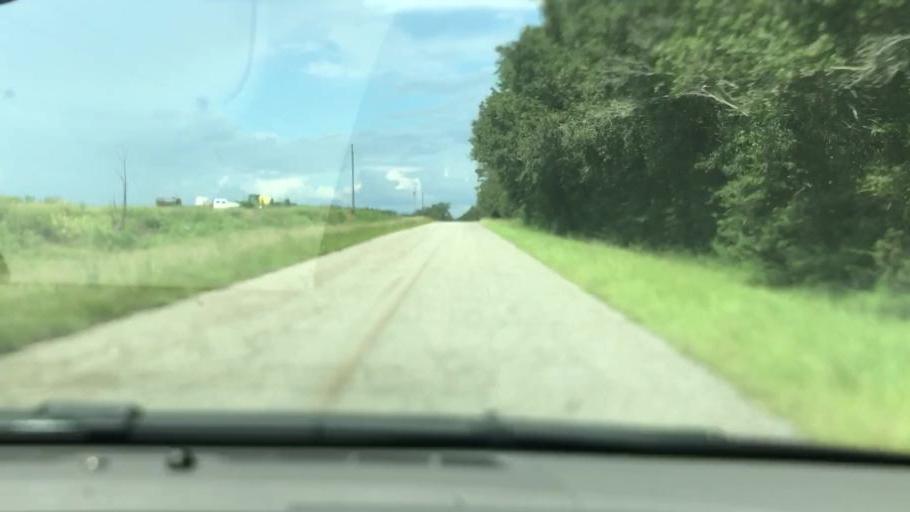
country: US
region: Georgia
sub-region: Early County
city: Blakely
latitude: 31.2089
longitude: -85.0034
